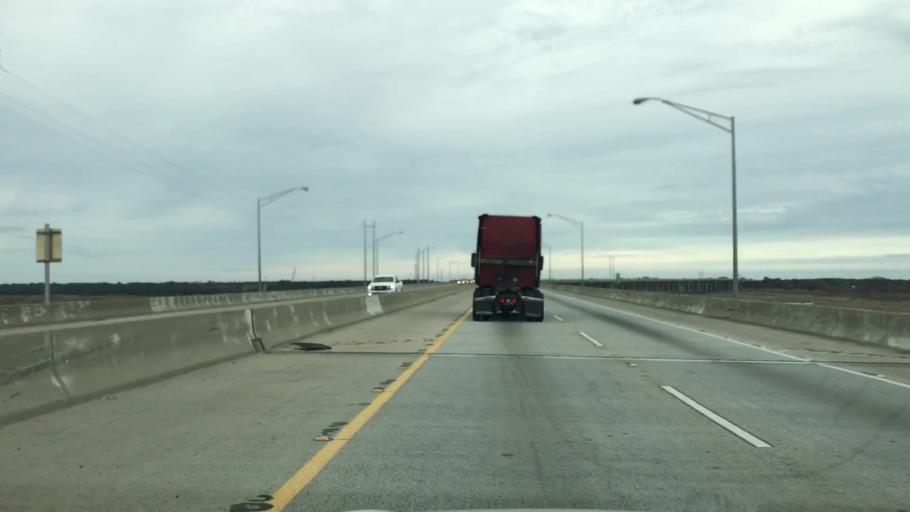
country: US
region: South Carolina
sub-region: Charleston County
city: North Charleston
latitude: 32.8897
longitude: -79.9531
